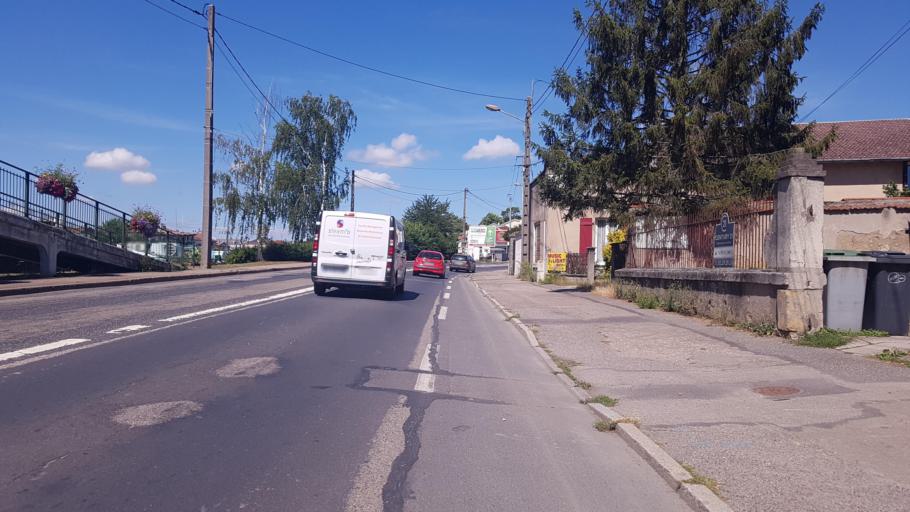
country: FR
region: Lorraine
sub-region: Departement de Meurthe-et-Moselle
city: Varangeville
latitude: 48.6351
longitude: 6.3165
